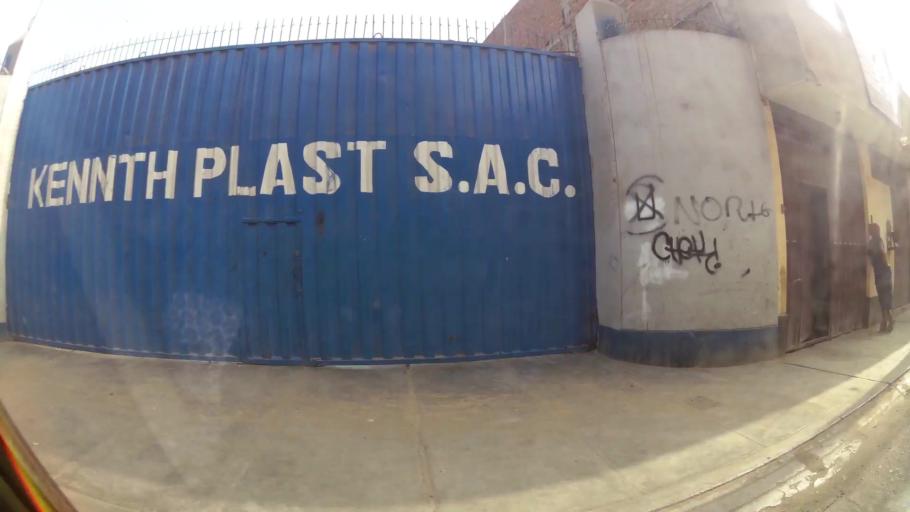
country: PE
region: La Libertad
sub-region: Provincia de Trujillo
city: Trujillo
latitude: -8.1069
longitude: -79.0183
